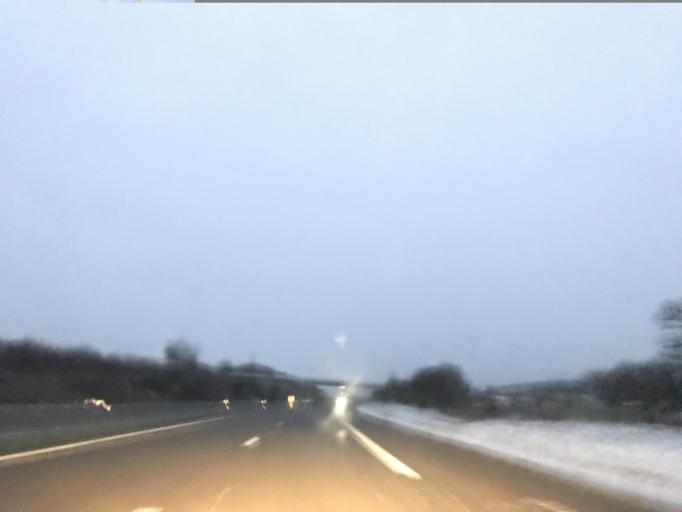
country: FR
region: Auvergne
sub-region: Departement du Puy-de-Dome
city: Saint-Ours
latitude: 45.8594
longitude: 2.8712
